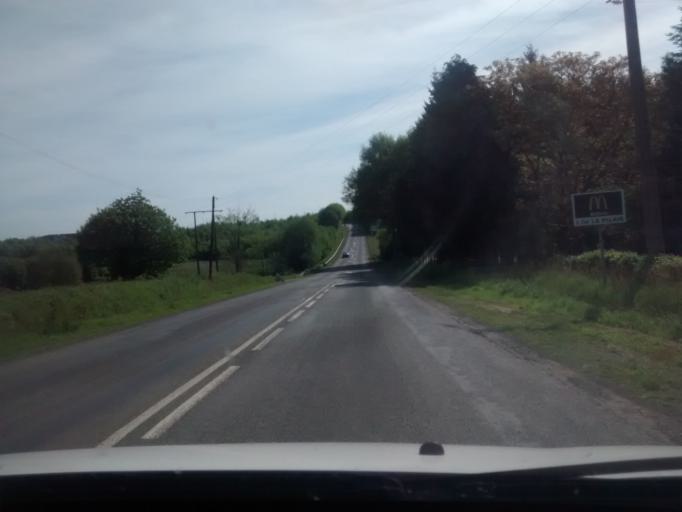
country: FR
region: Brittany
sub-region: Departement d'Ille-et-Vilaine
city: Lecousse
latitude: 48.3504
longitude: -1.2403
